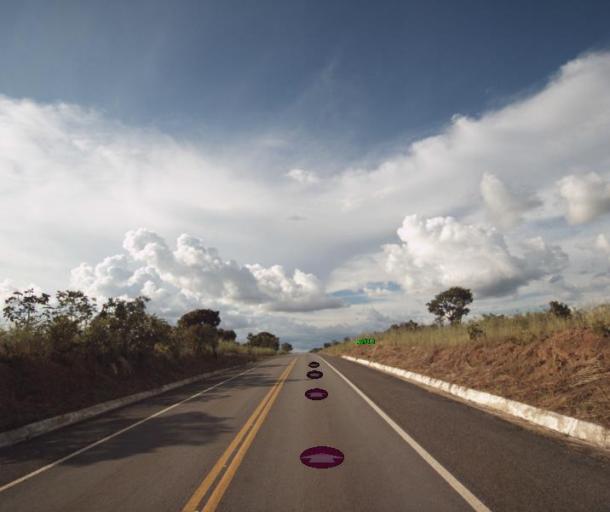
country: BR
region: Goias
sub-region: Barro Alto
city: Barro Alto
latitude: -14.8423
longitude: -48.6384
